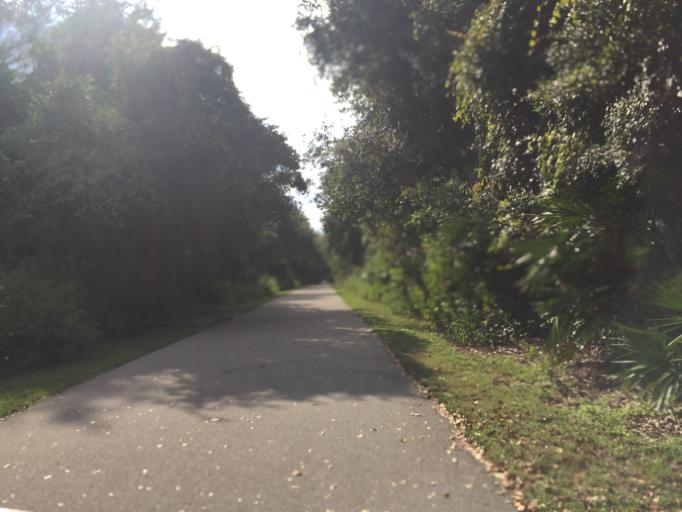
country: US
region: Florida
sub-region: Seminole County
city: Oviedo
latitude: 28.6856
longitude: -81.2422
